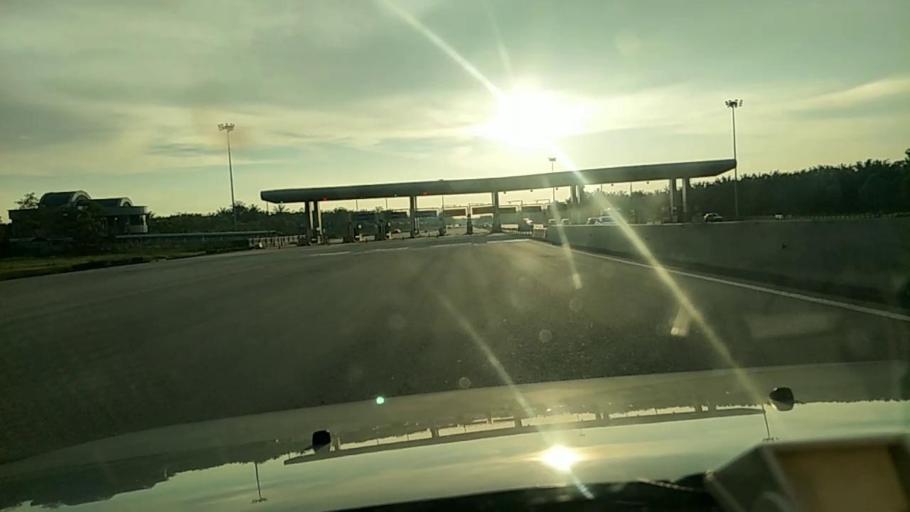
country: MY
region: Selangor
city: Batu Arang
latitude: 3.2904
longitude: 101.3943
